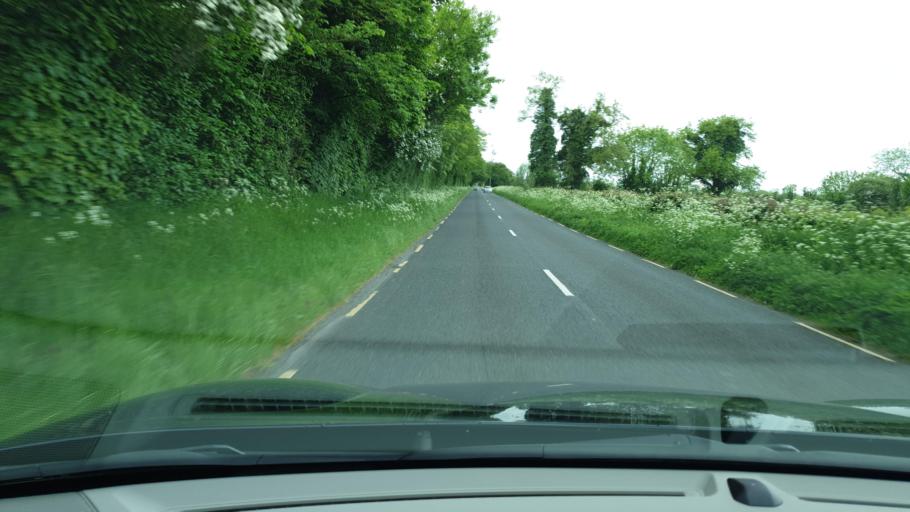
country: IE
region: Leinster
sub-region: An Mhi
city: Ratoath
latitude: 53.5174
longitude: -6.4721
